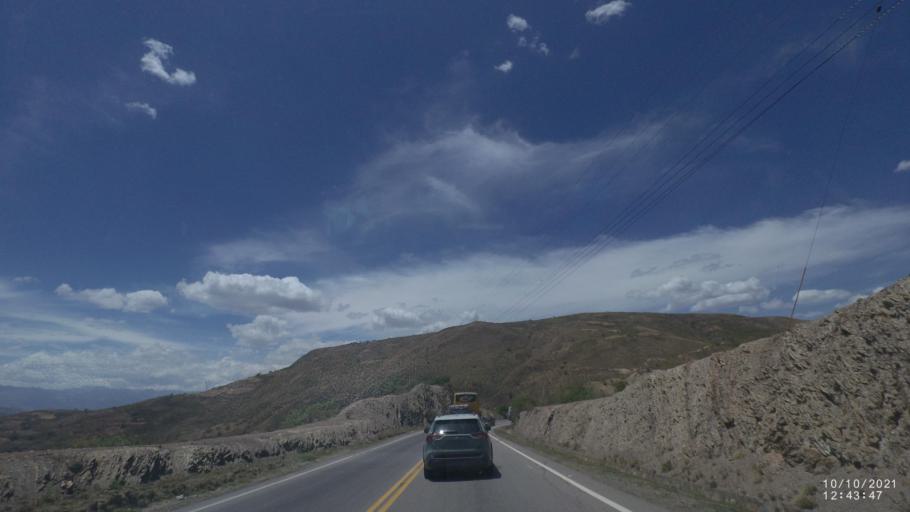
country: BO
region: Cochabamba
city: Irpa Irpa
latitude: -17.6303
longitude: -66.3824
